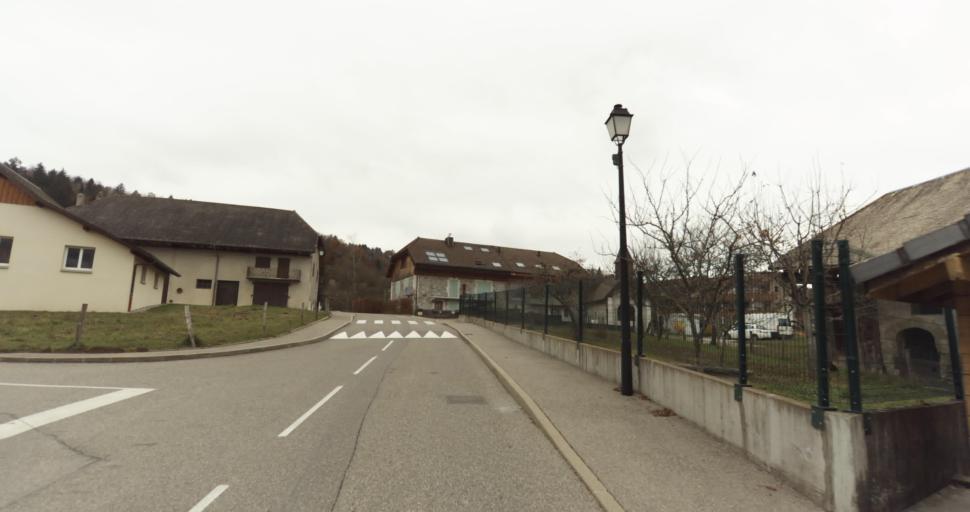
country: FR
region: Rhone-Alpes
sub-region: Departement de la Haute-Savoie
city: Saint-Martin-Bellevue
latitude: 45.9651
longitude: 6.1609
